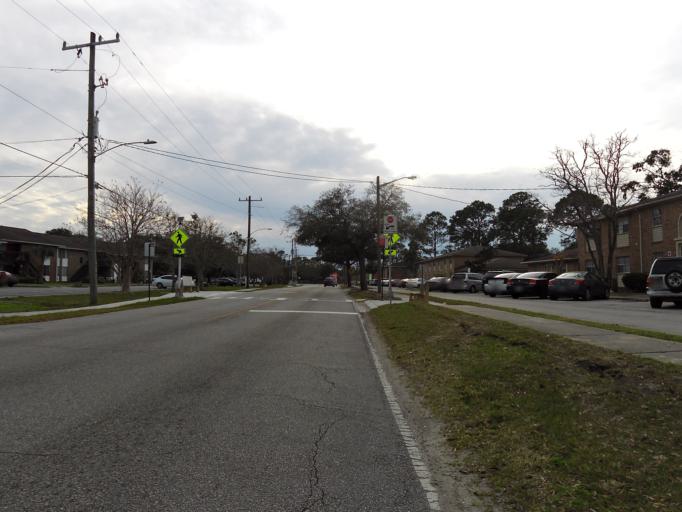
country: US
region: Florida
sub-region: Duval County
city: Jacksonville
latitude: 30.2503
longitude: -81.6209
